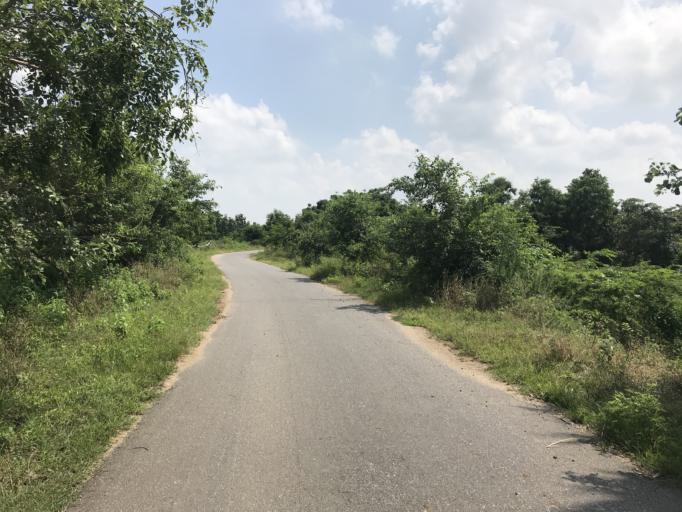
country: IN
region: Telangana
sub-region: Warangal
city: Mahbubabad
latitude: 17.6848
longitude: 79.7177
